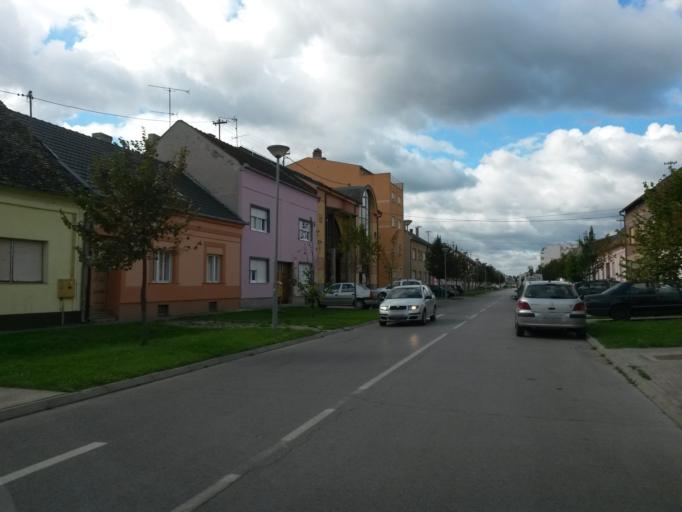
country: HR
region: Osjecko-Baranjska
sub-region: Grad Osijek
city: Osijek
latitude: 45.5569
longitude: 18.6696
